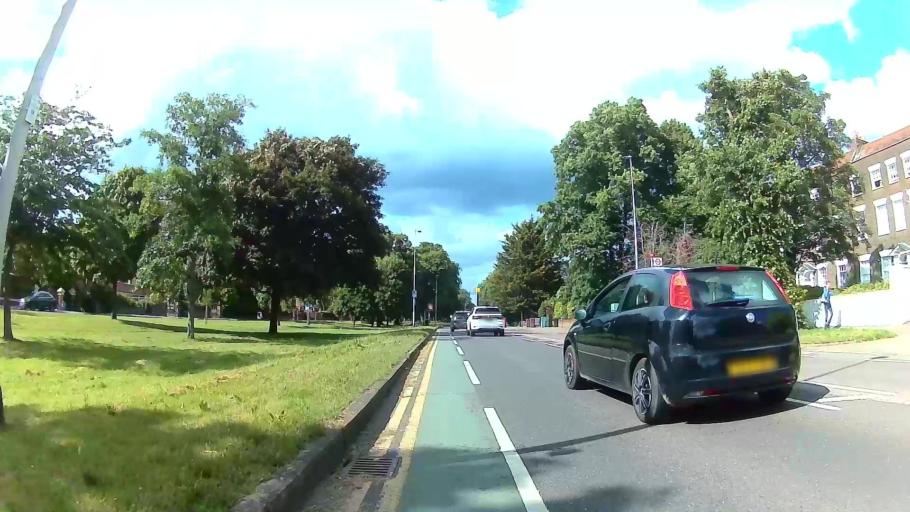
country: GB
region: England
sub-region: Greater London
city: Woodford Green
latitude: 51.5865
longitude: 0.0212
